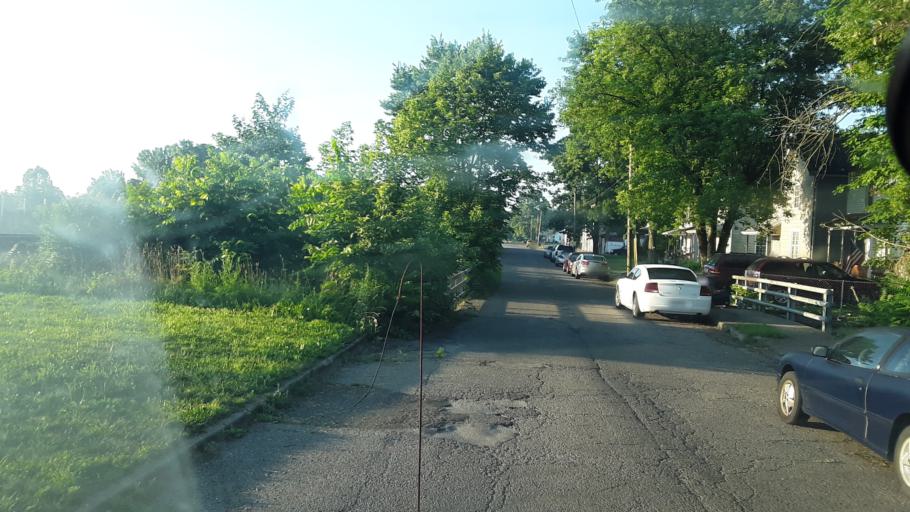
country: US
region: Ohio
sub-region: Licking County
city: Newark
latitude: 40.0665
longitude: -82.4054
